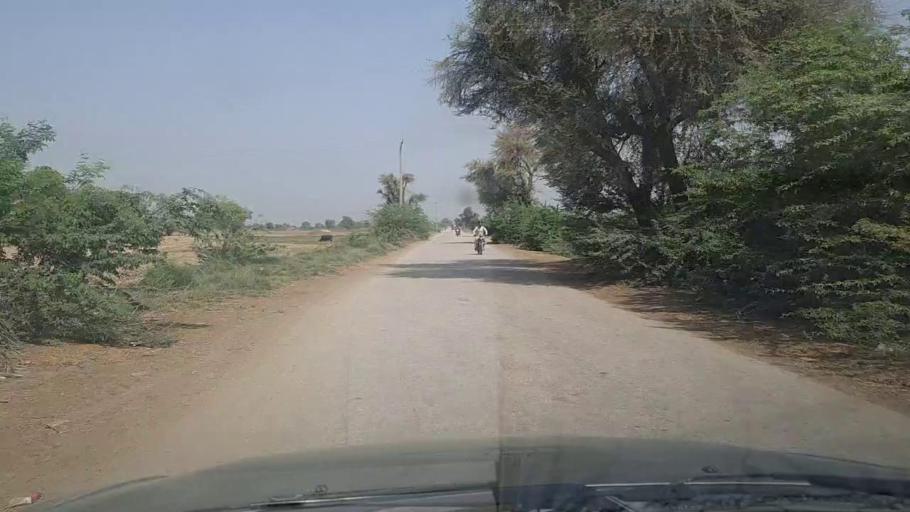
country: PK
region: Sindh
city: Setharja Old
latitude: 27.1339
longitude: 68.5307
